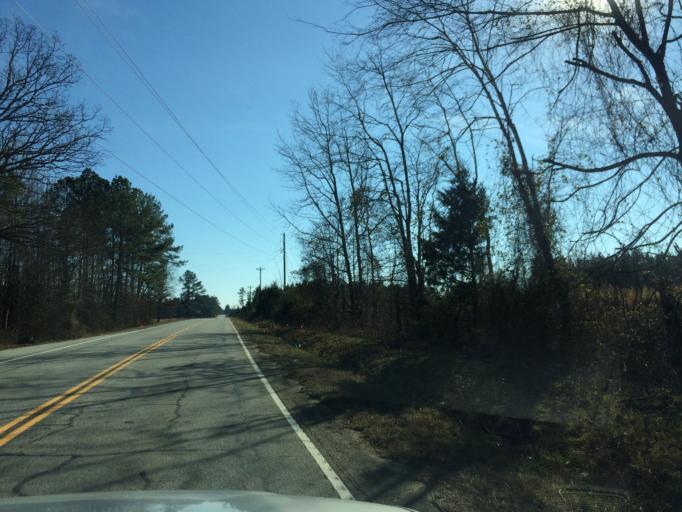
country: US
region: South Carolina
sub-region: Greenwood County
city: Ninety Six
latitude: 34.3140
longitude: -82.0492
